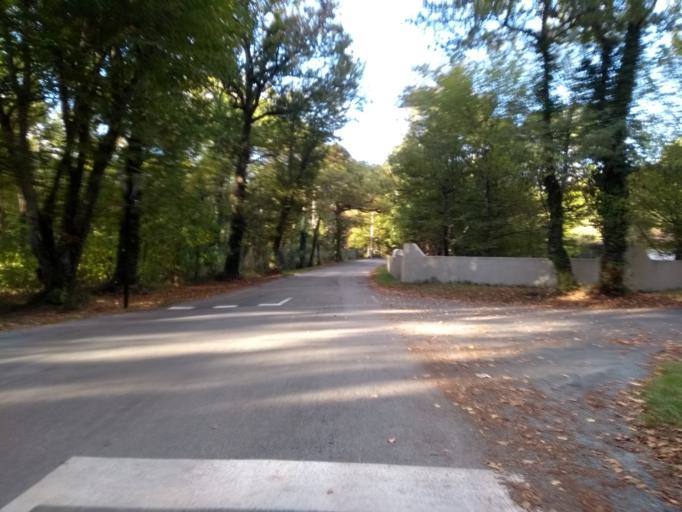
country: FR
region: Aquitaine
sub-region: Departement de la Gironde
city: Canejan
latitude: 44.7529
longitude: -0.6256
